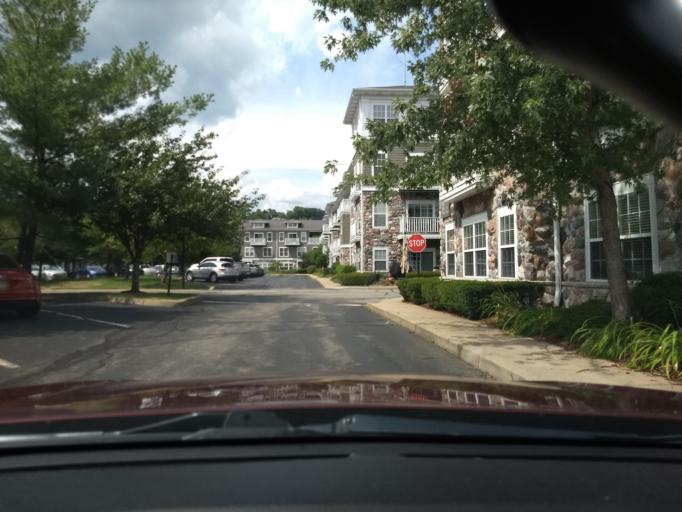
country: US
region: Pennsylvania
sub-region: Allegheny County
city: Blawnox
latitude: 40.4861
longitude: -79.8742
